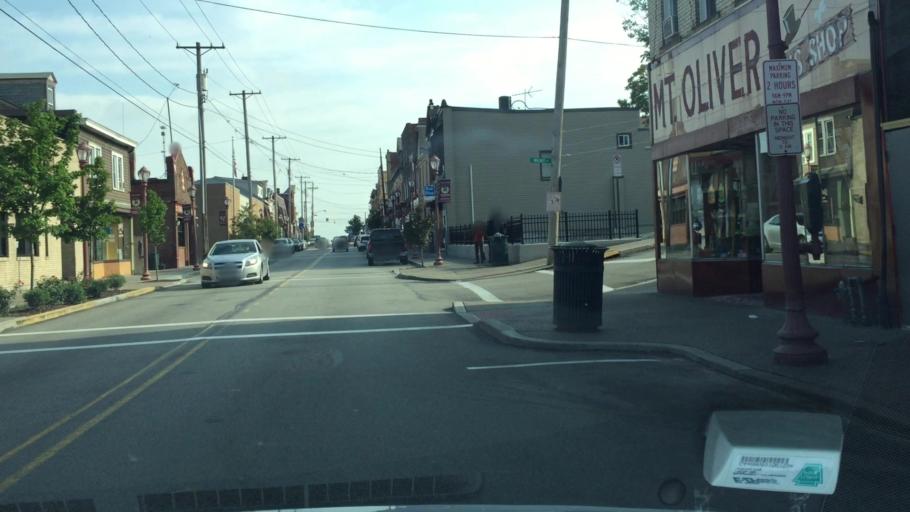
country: US
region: Pennsylvania
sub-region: Allegheny County
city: Mount Oliver
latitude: 40.4157
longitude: -79.9872
